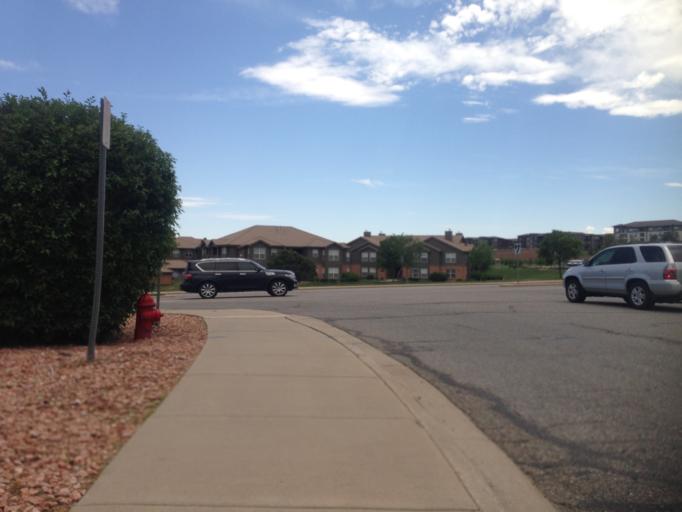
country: US
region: Colorado
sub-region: Boulder County
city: Superior
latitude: 39.9304
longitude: -105.1478
